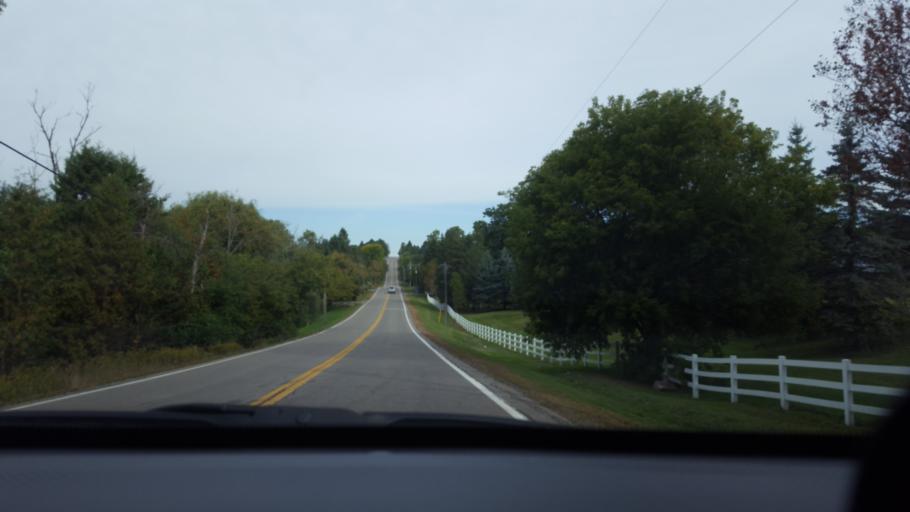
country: CA
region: Ontario
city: Newmarket
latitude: 43.9776
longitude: -79.5417
